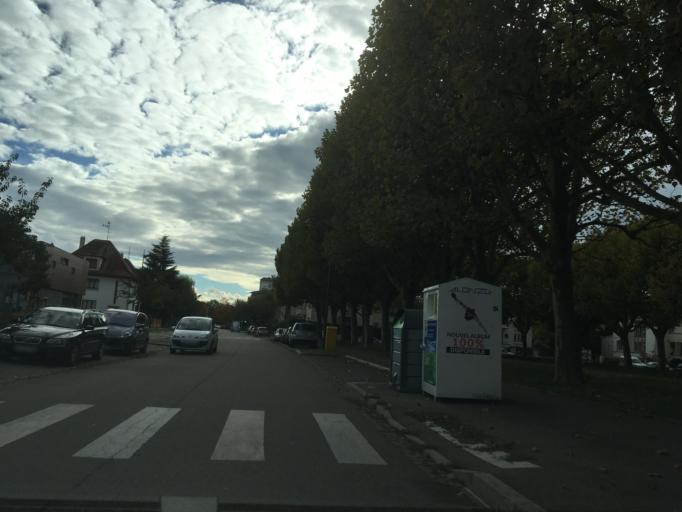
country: FR
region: Alsace
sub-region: Departement du Bas-Rhin
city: Strasbourg
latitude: 48.5536
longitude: 7.7526
